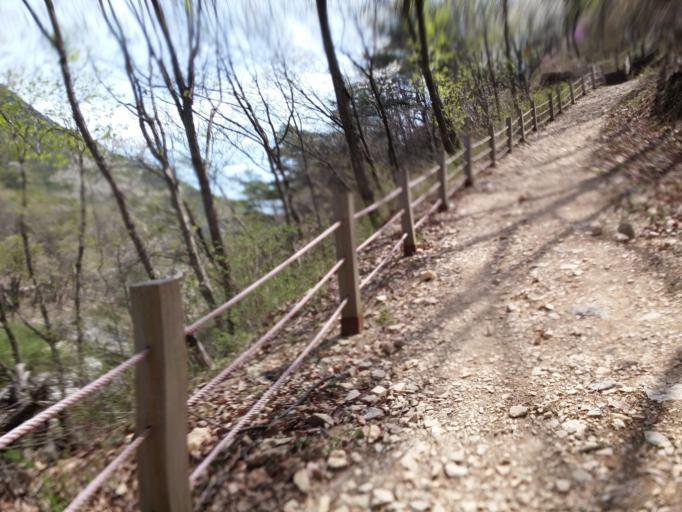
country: KR
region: Chungcheongbuk-do
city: Okcheon
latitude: 36.2355
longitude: 127.5601
